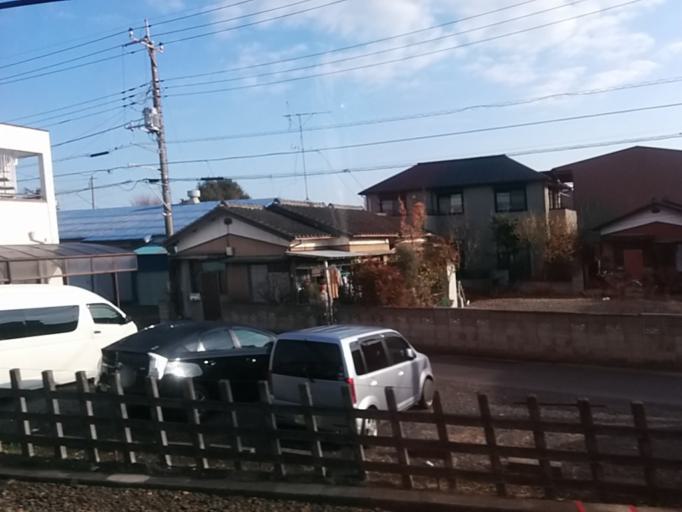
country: JP
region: Saitama
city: Oi
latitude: 35.8560
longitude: 139.5273
